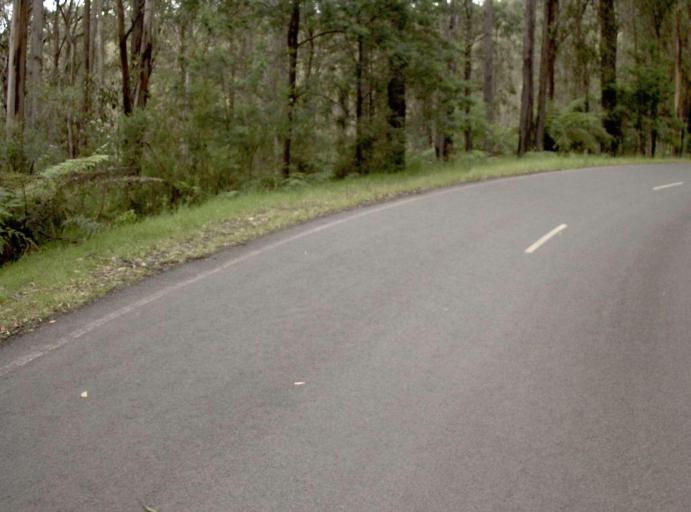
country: AU
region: Victoria
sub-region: Latrobe
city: Moe
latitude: -37.9342
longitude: 146.1152
